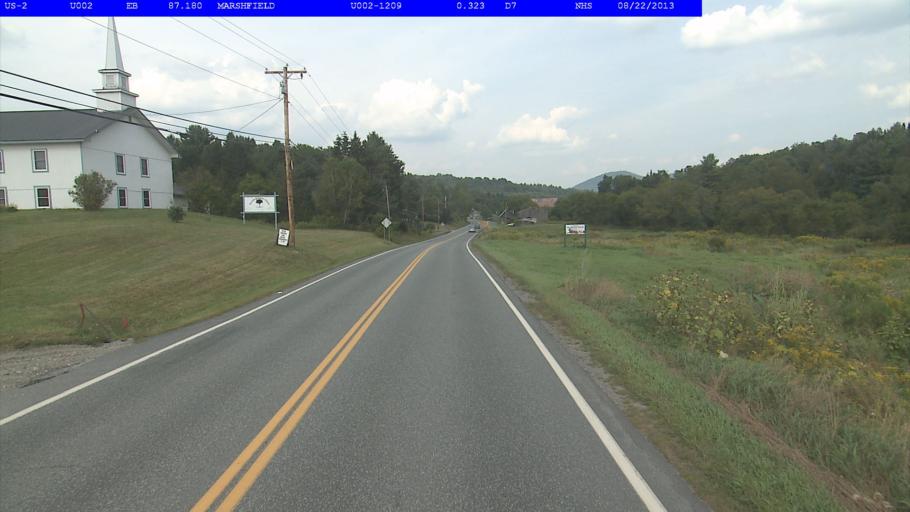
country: US
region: Vermont
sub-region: Washington County
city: Barre
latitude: 44.2825
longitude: -72.4171
